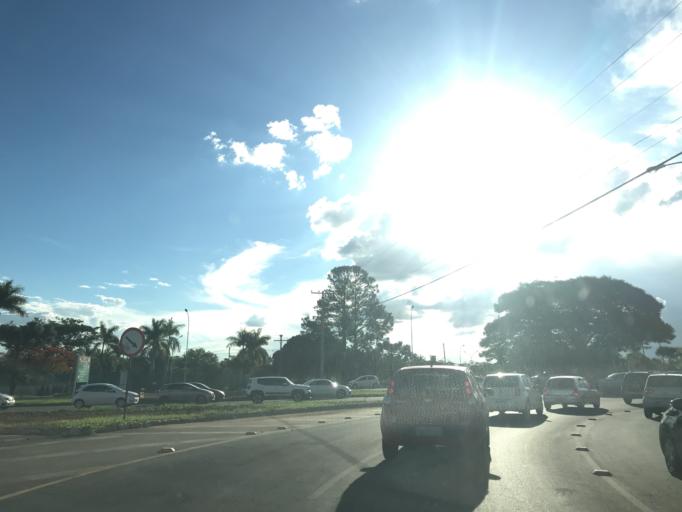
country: BR
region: Federal District
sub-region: Brasilia
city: Brasilia
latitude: -15.8080
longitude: -47.9272
